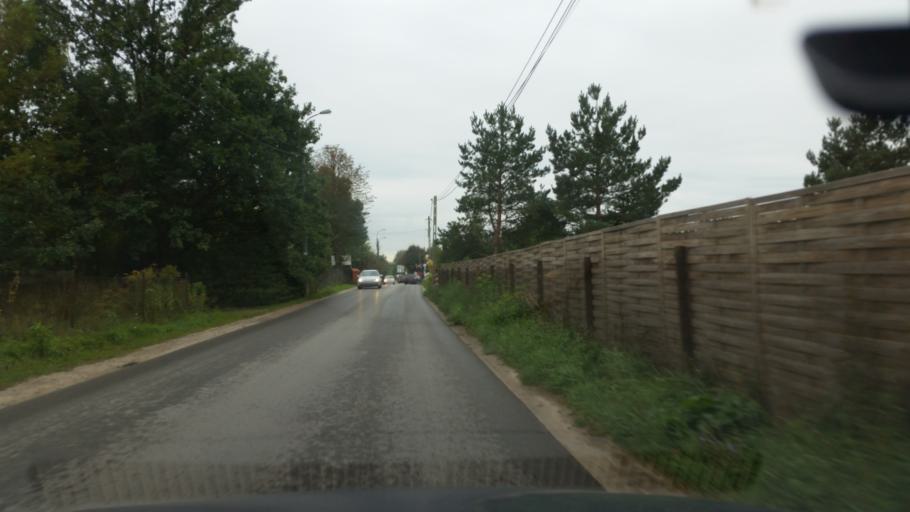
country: PL
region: Masovian Voivodeship
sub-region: Warszawa
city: Kabaty
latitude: 52.0973
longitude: 21.0793
